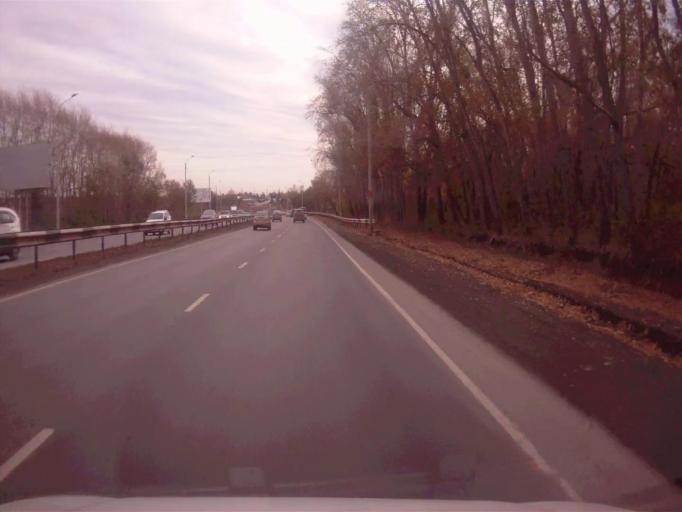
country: RU
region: Chelyabinsk
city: Novosineglazovskiy
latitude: 55.0494
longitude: 61.4140
